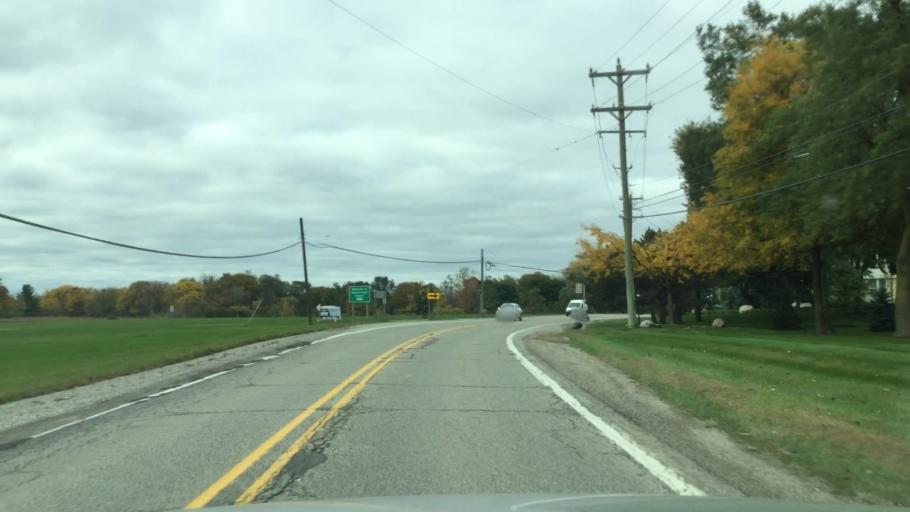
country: US
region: Michigan
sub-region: Macomb County
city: Romeo
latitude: 42.8035
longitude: -82.9765
